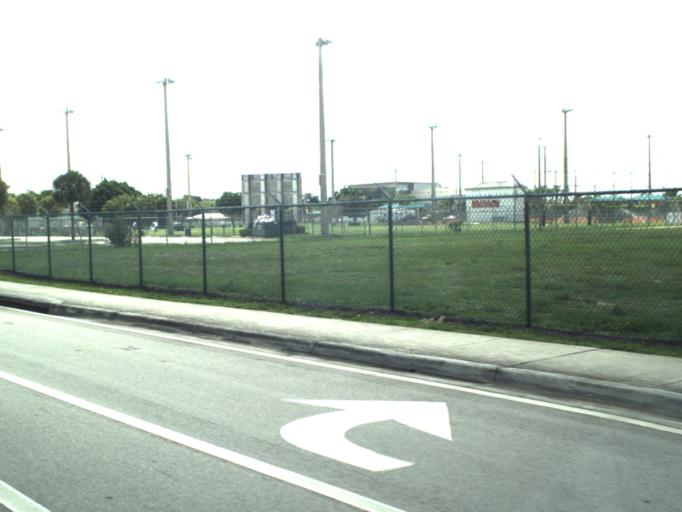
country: US
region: Florida
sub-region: Broward County
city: Pembroke Pines
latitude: 26.0093
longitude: -80.2391
